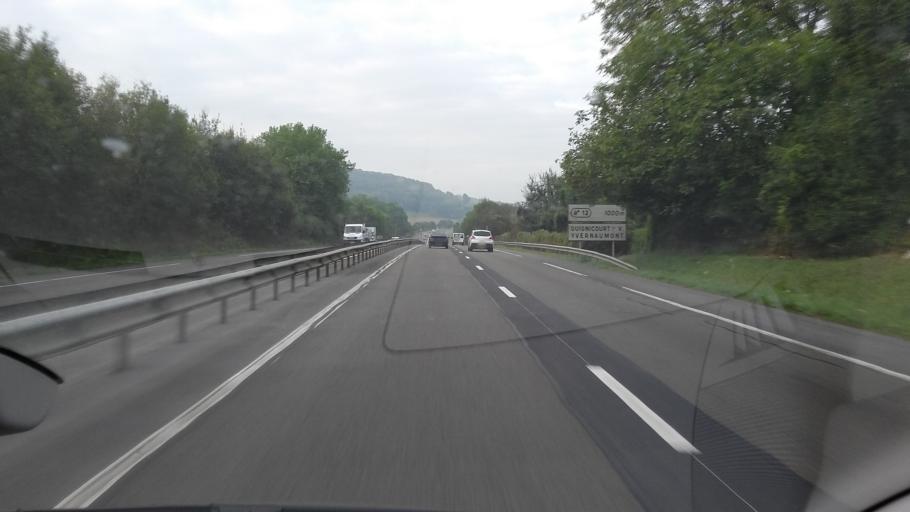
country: FR
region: Champagne-Ardenne
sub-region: Departement des Ardennes
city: La Francheville
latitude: 49.6890
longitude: 4.6749
